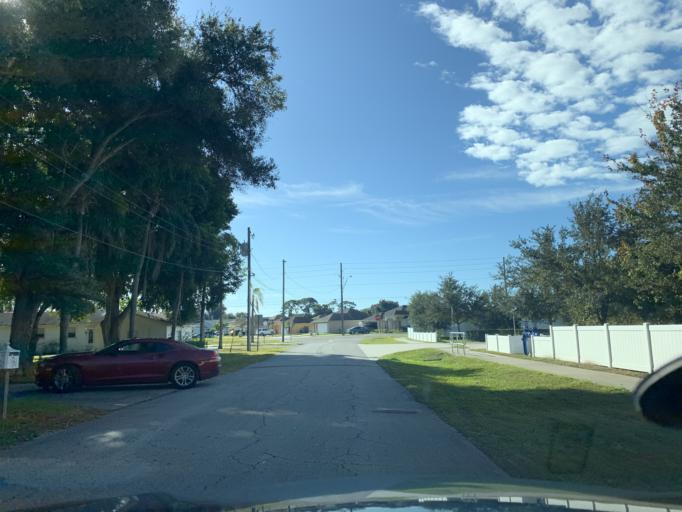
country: US
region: Florida
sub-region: Pinellas County
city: Kenneth City
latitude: 27.8144
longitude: -82.7377
